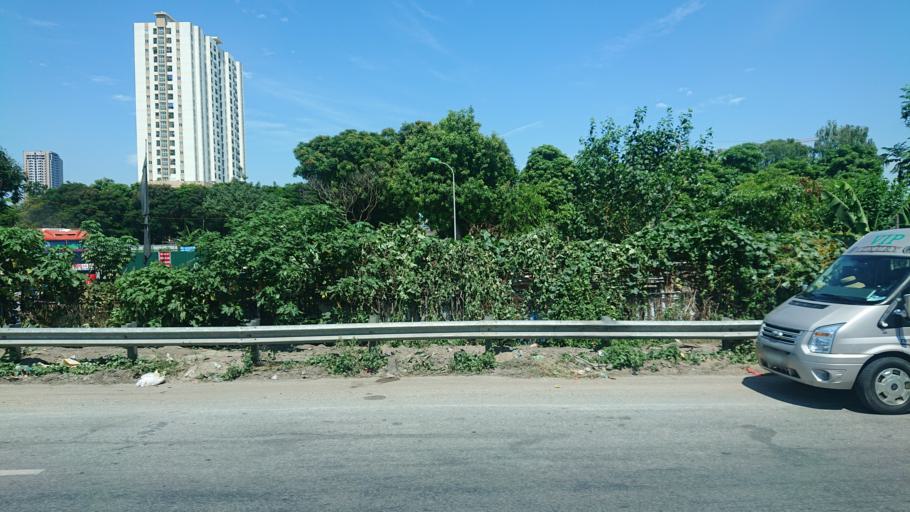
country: VN
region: Ha Noi
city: Van Dien
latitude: 20.9634
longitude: 105.8472
